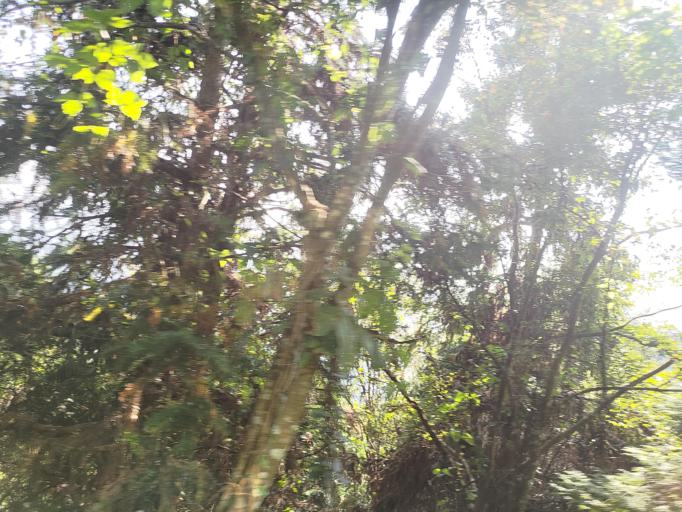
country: TW
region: Taiwan
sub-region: Hsinchu
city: Hsinchu
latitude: 24.6030
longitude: 121.0929
